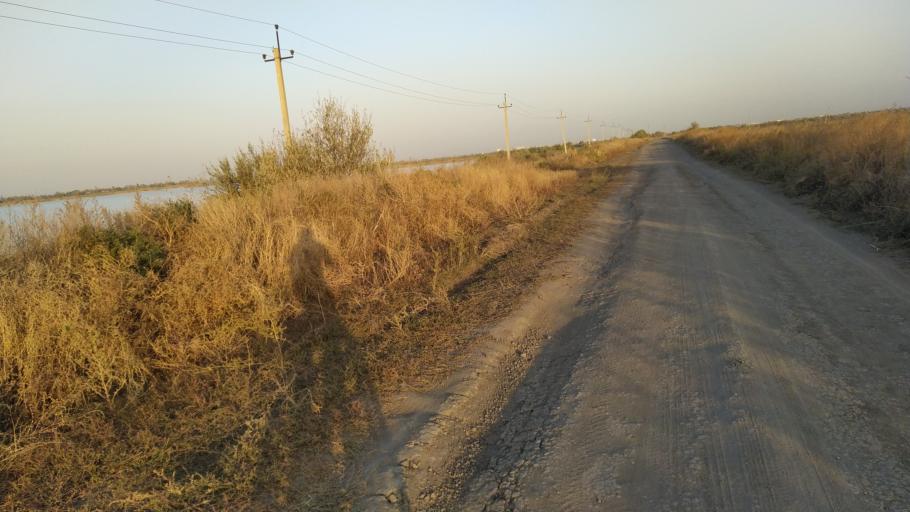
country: RU
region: Rostov
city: Bataysk
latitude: 47.1379
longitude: 39.6463
